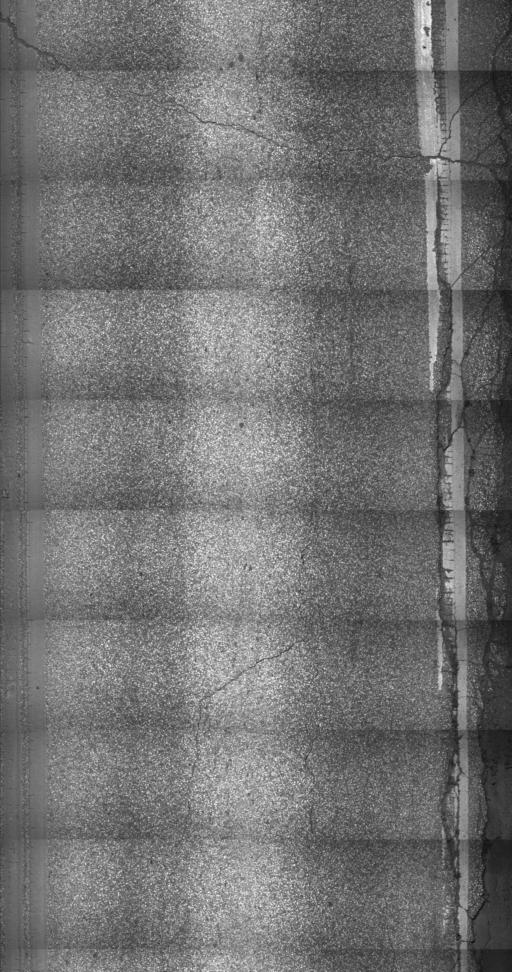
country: US
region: Vermont
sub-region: Rutland County
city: Fair Haven
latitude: 43.5825
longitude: -73.2648
